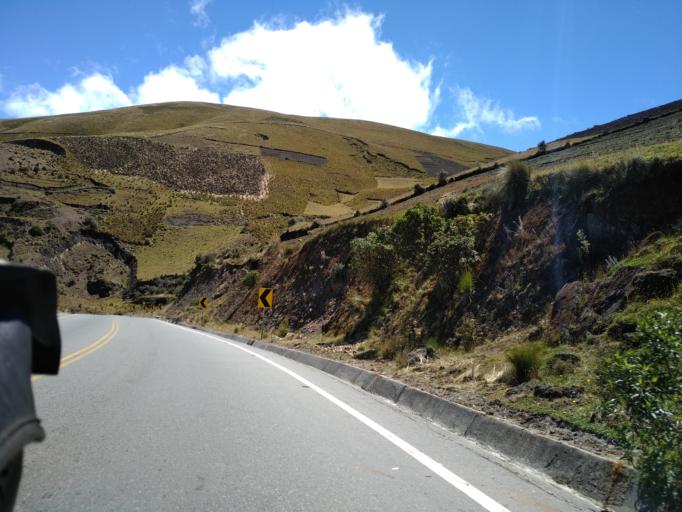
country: EC
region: Cotopaxi
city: Pujili
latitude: -0.9867
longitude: -78.9480
